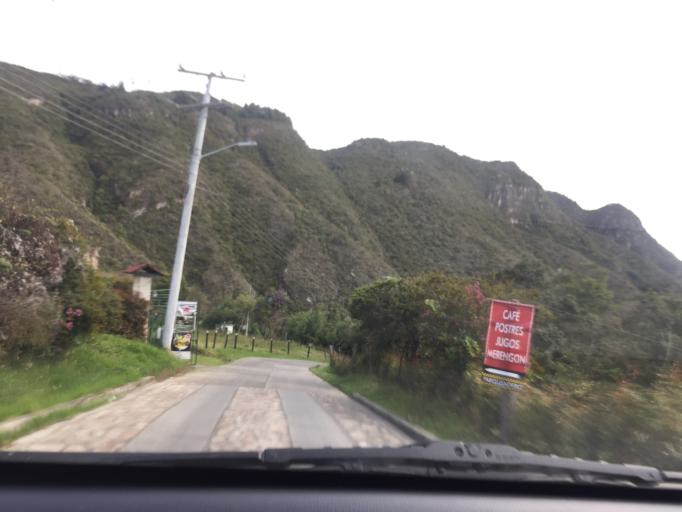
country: CO
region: Cundinamarca
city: Sopo
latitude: 4.9144
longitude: -73.9251
